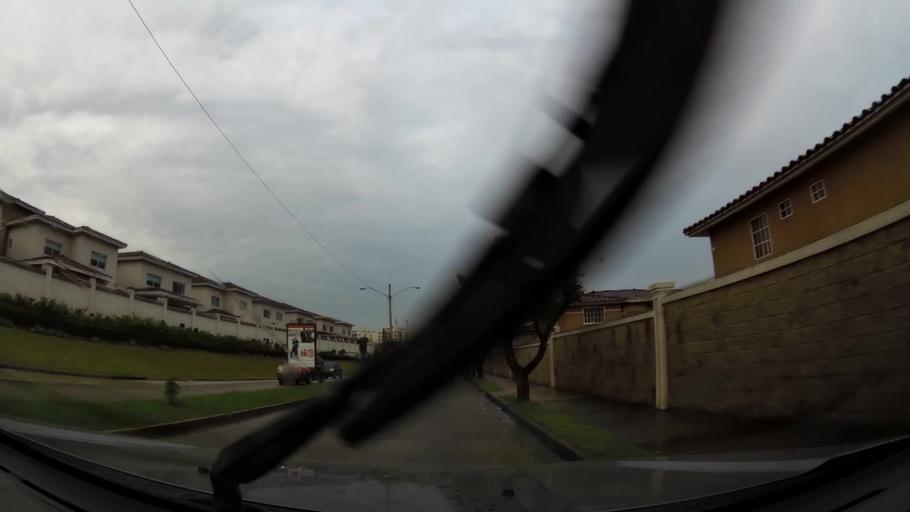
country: PA
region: Panama
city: Panama
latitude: 9.0340
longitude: -79.5327
